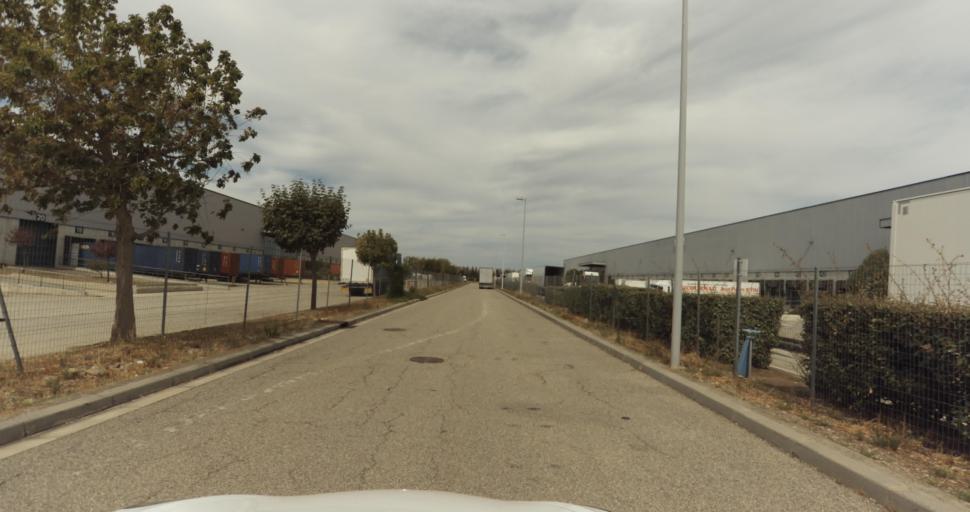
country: FR
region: Provence-Alpes-Cote d'Azur
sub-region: Departement des Bouches-du-Rhone
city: Miramas
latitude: 43.6092
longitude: 4.9968
